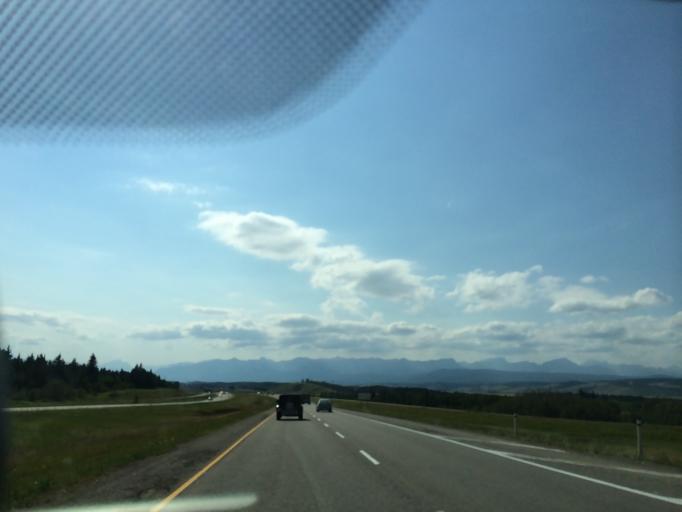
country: CA
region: Alberta
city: Cochrane
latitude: 51.1618
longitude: -114.7725
